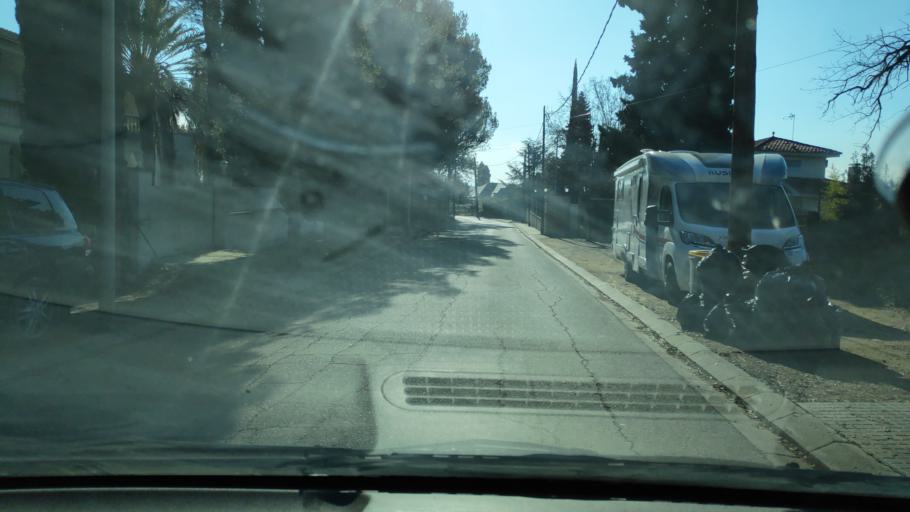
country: ES
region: Catalonia
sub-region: Provincia de Barcelona
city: Sant Quirze del Valles
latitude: 41.5041
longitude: 2.0788
